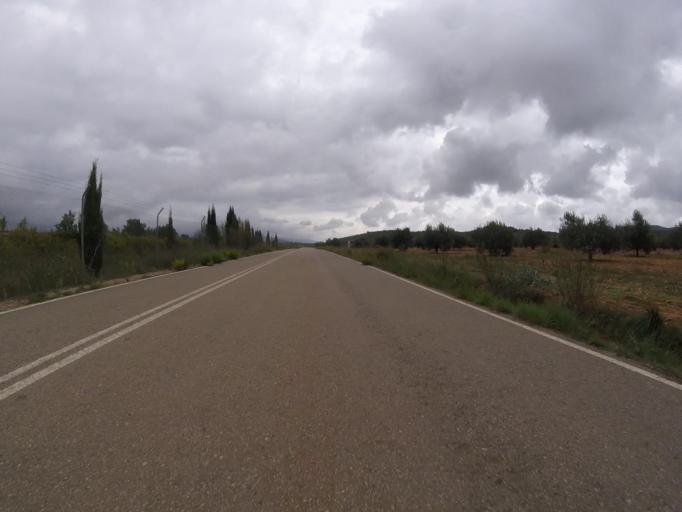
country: ES
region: Valencia
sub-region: Provincia de Castello
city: Cabanes
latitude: 40.1780
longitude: 0.0450
